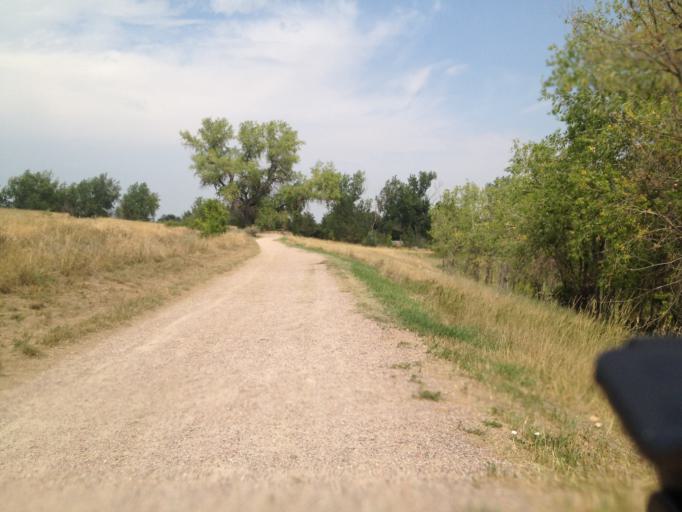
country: US
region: Colorado
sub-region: Boulder County
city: Louisville
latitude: 39.9841
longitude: -105.1481
